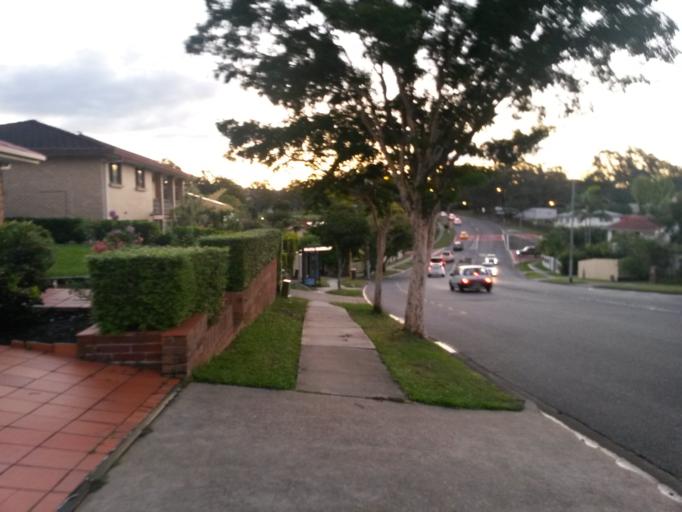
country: AU
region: Queensland
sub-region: Brisbane
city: Camp Hill
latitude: -27.5034
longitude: 153.0869
